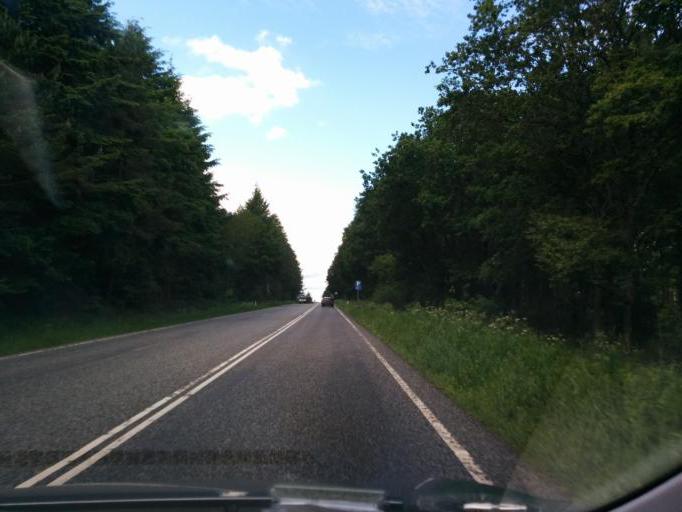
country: DK
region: Central Jutland
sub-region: Syddjurs Kommune
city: Ebeltoft
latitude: 56.2536
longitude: 10.6375
